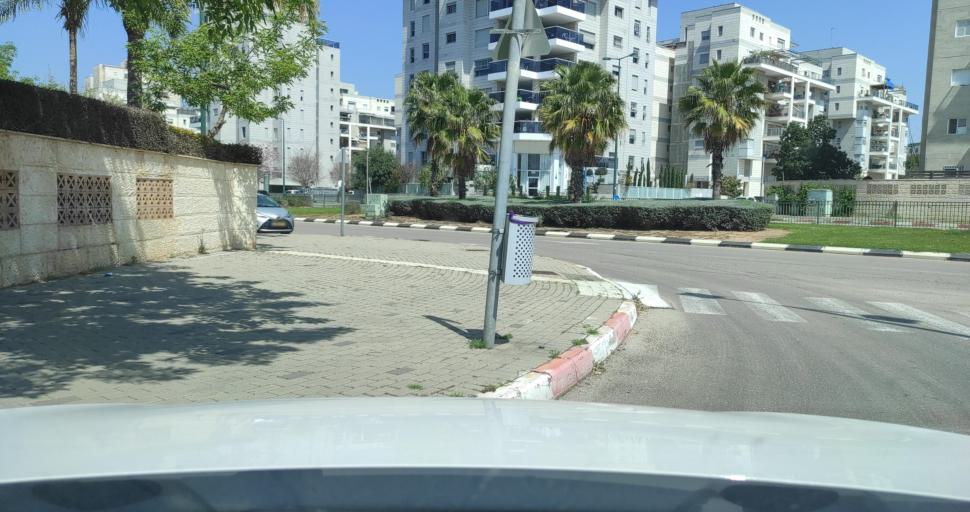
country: IL
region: Central District
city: Nordiyya
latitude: 32.2965
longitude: 34.8731
